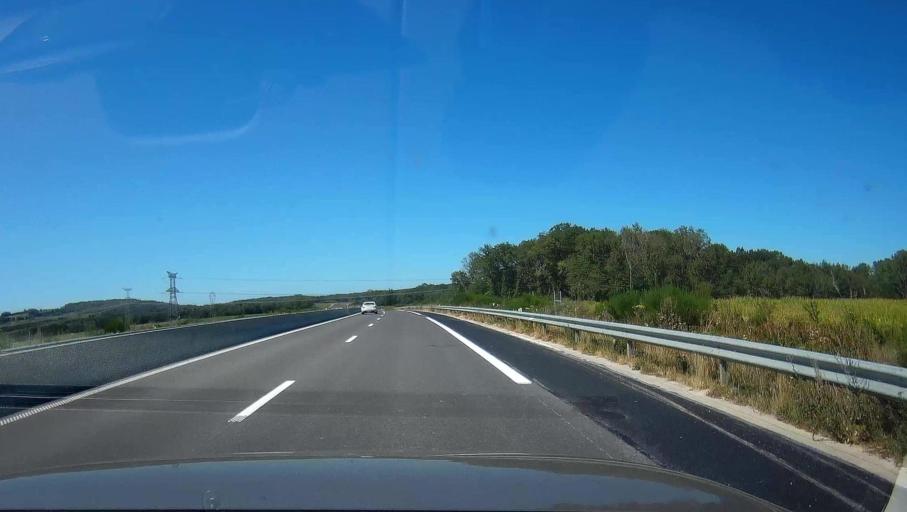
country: FR
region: Champagne-Ardenne
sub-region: Departement des Ardennes
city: Rimogne
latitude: 49.8009
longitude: 4.5328
